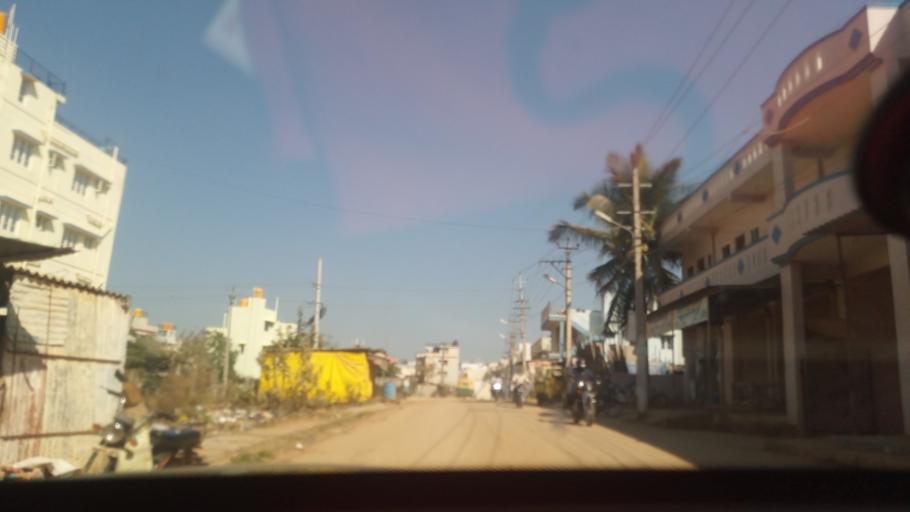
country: IN
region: Karnataka
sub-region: Bangalore Rural
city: Nelamangala
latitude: 13.0368
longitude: 77.4889
